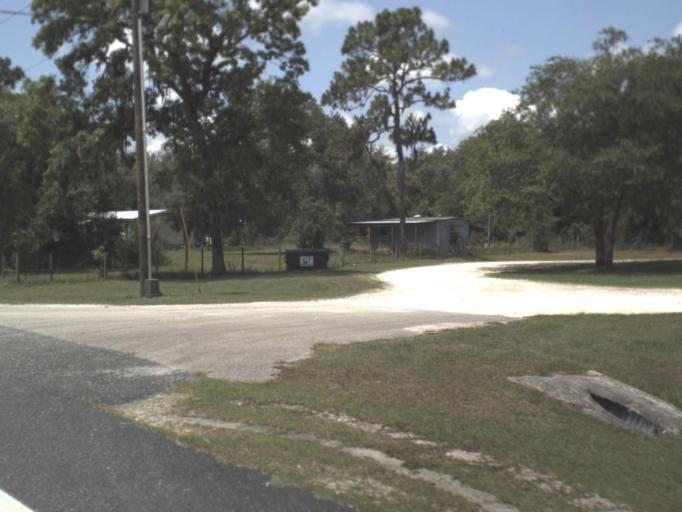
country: US
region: Florida
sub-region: Levy County
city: Williston Highlands
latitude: 29.2922
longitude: -82.5343
